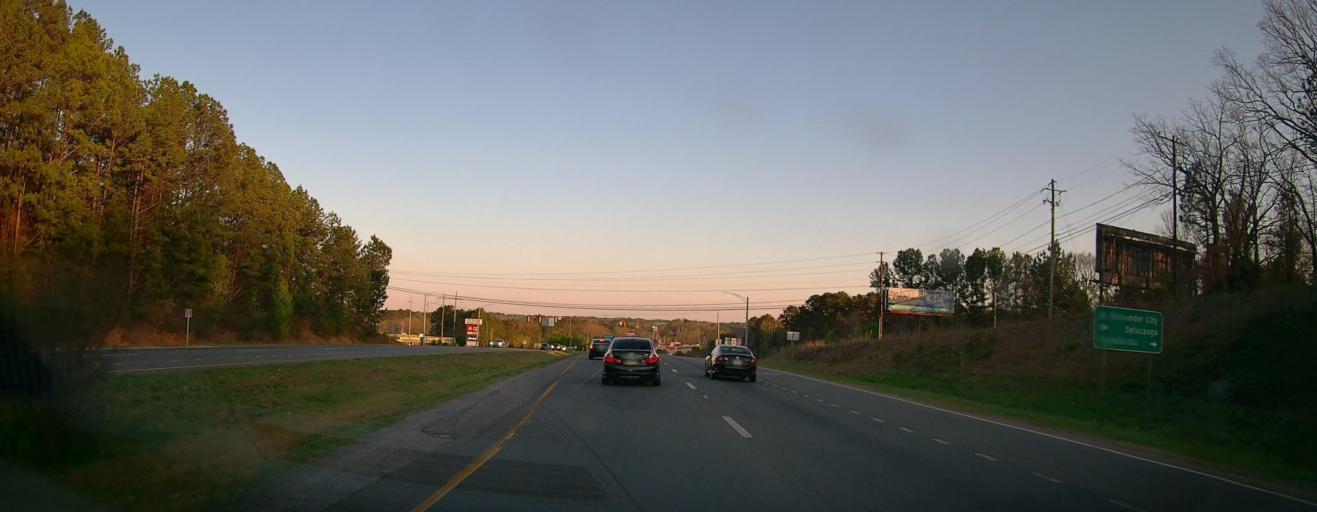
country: US
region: Alabama
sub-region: Talladega County
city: Mignon
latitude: 33.1649
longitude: -86.2765
